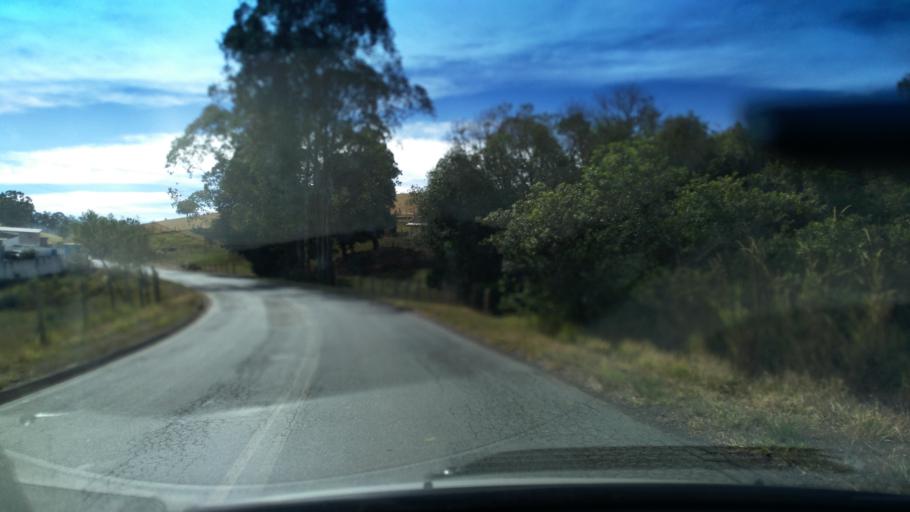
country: BR
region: Minas Gerais
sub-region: Andradas
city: Andradas
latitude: -22.0417
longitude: -46.3519
